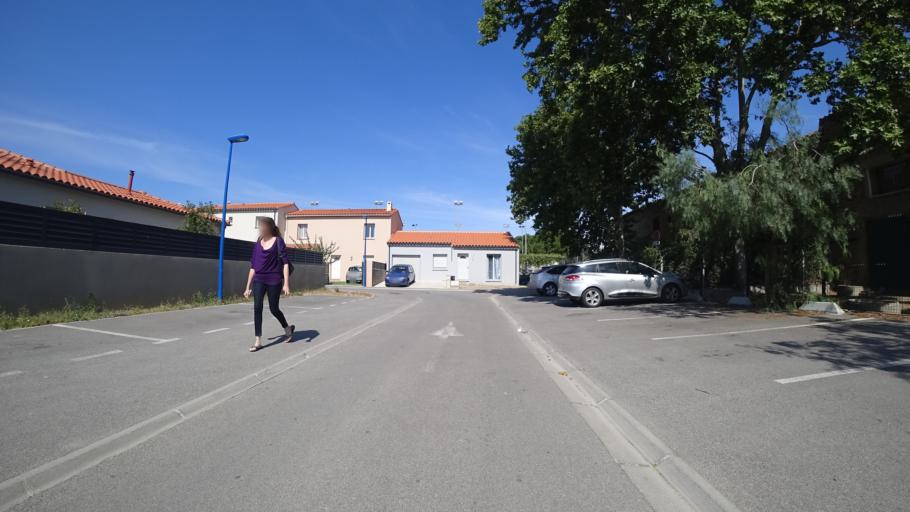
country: FR
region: Languedoc-Roussillon
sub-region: Departement des Pyrenees-Orientales
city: Peyrestortes
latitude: 42.7761
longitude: 2.8376
